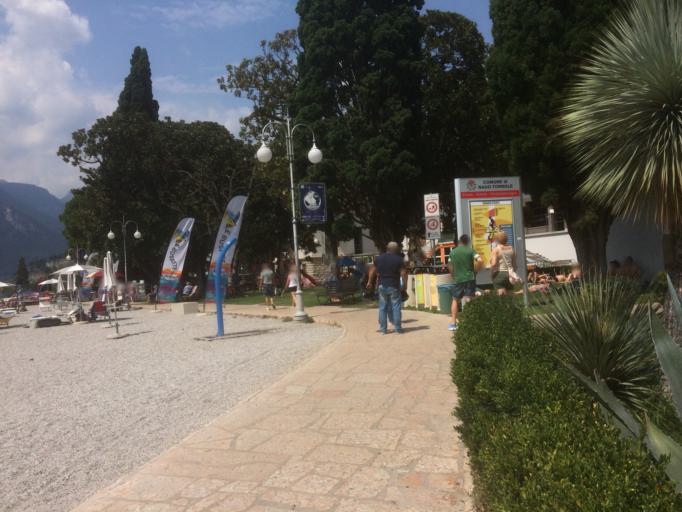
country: IT
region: Trentino-Alto Adige
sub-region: Provincia di Trento
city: Torbole sul Garda
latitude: 45.8692
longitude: 10.8742
